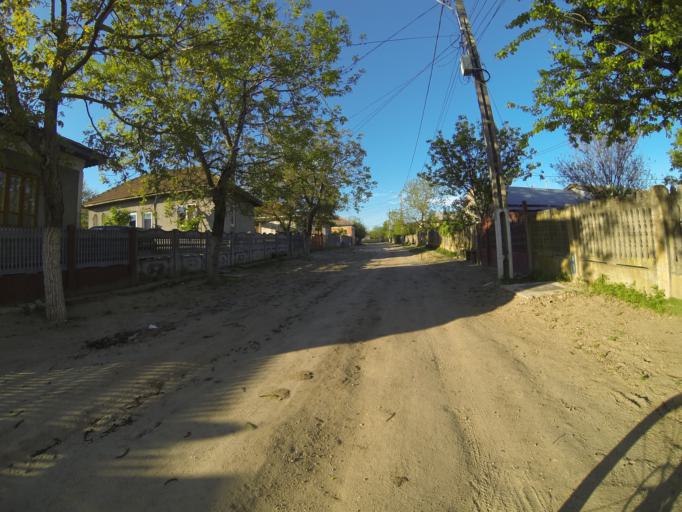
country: RO
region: Dolj
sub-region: Comuna Segarcea
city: Segarcea
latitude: 44.0942
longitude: 23.7373
